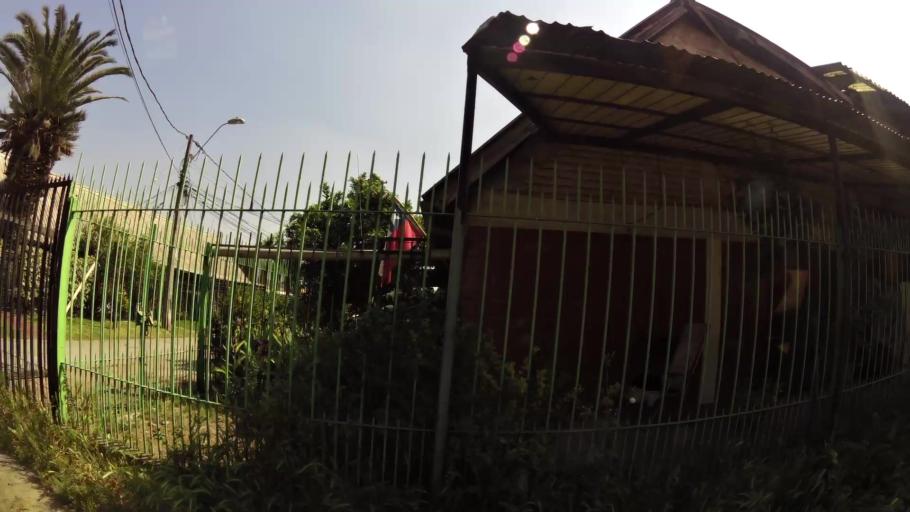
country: CL
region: Santiago Metropolitan
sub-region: Provincia de Santiago
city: La Pintana
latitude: -33.5500
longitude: -70.6096
